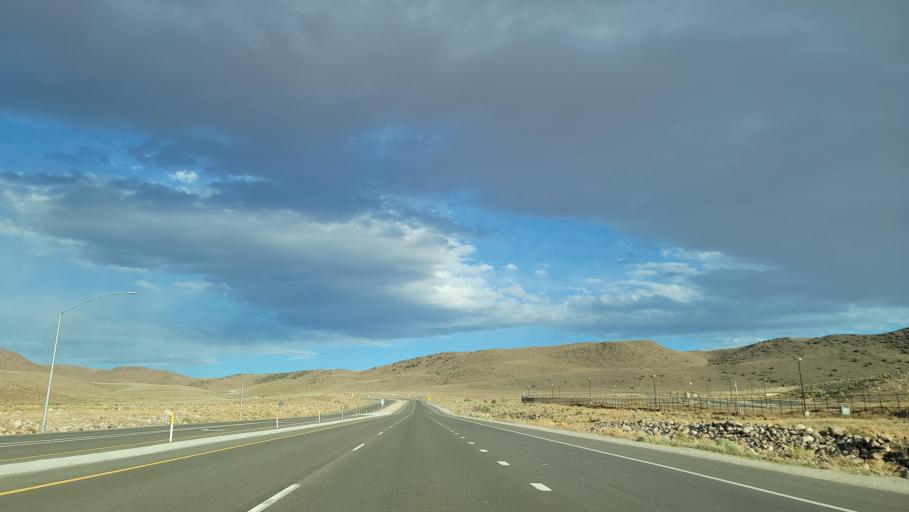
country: US
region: Nevada
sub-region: Lyon County
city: Stagecoach
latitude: 39.5005
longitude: -119.4279
